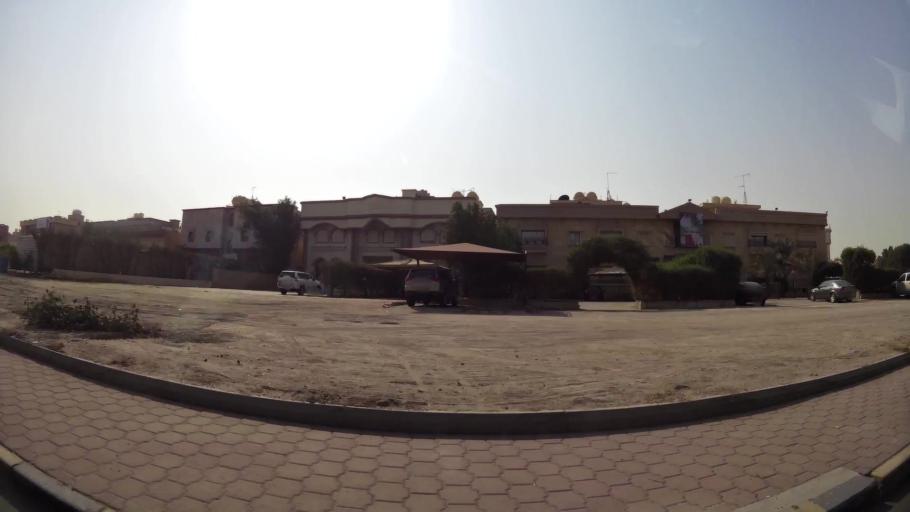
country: KW
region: Al Asimah
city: Ar Rabiyah
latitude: 29.2764
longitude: 47.8950
